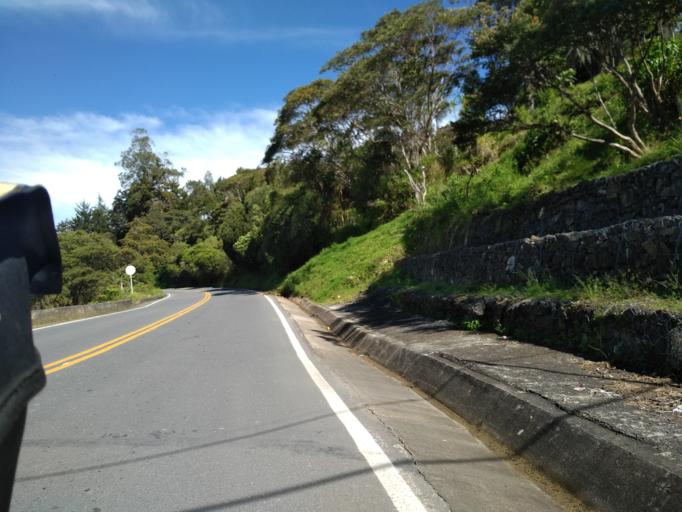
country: CO
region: Santander
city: Velez
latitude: 5.9986
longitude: -73.6855
